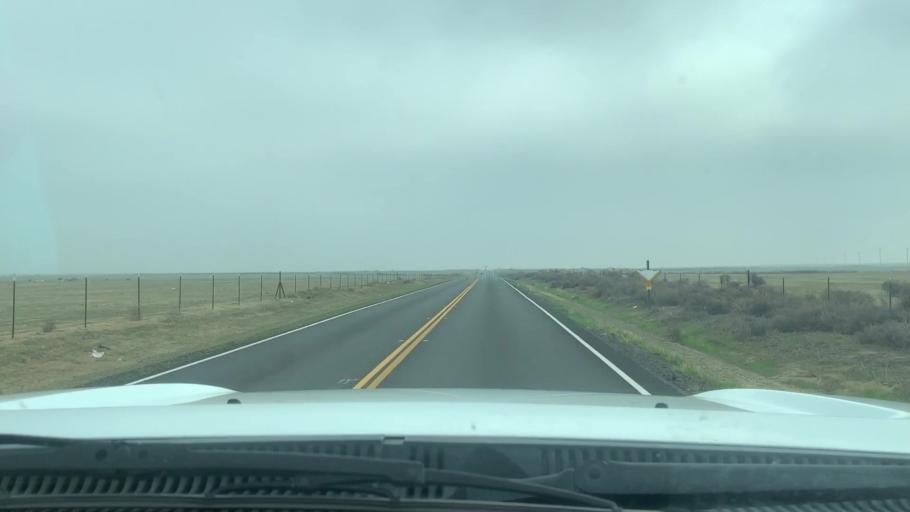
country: US
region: California
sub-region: Kern County
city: Lost Hills
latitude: 35.5879
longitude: -119.8346
